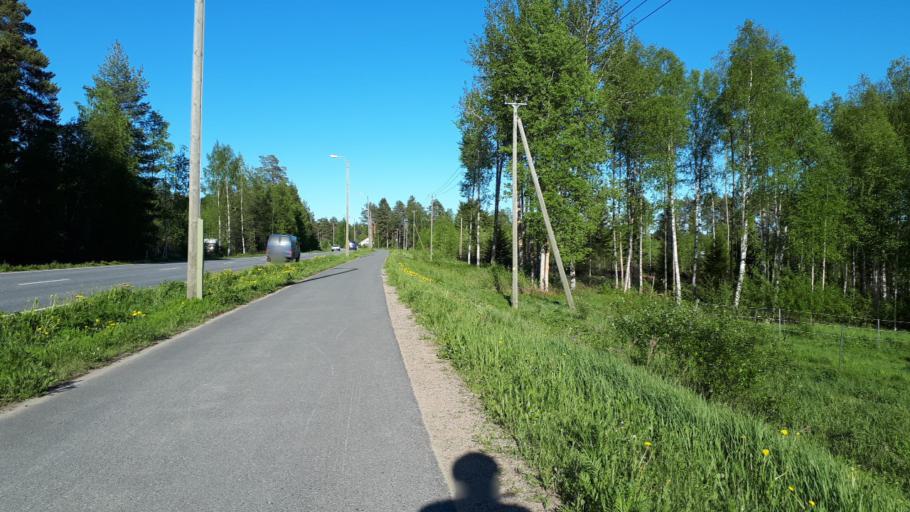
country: FI
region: Northern Ostrobothnia
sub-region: Oulunkaari
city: Ii
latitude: 65.3250
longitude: 25.5011
